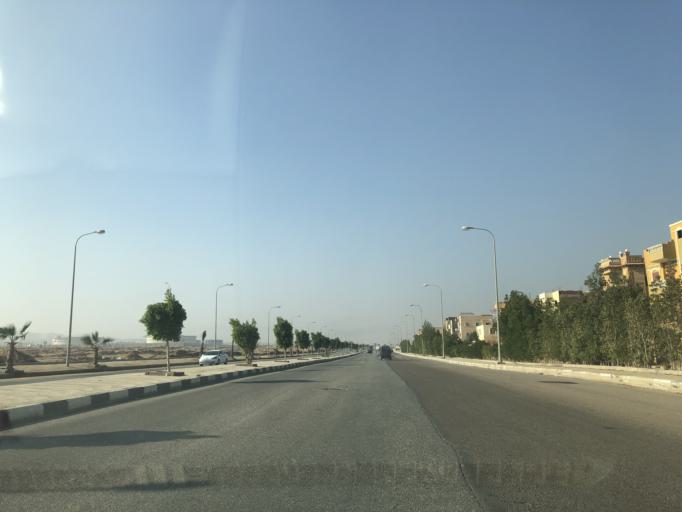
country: EG
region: Al Jizah
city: Madinat Sittah Uktubar
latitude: 29.9297
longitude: 31.0481
